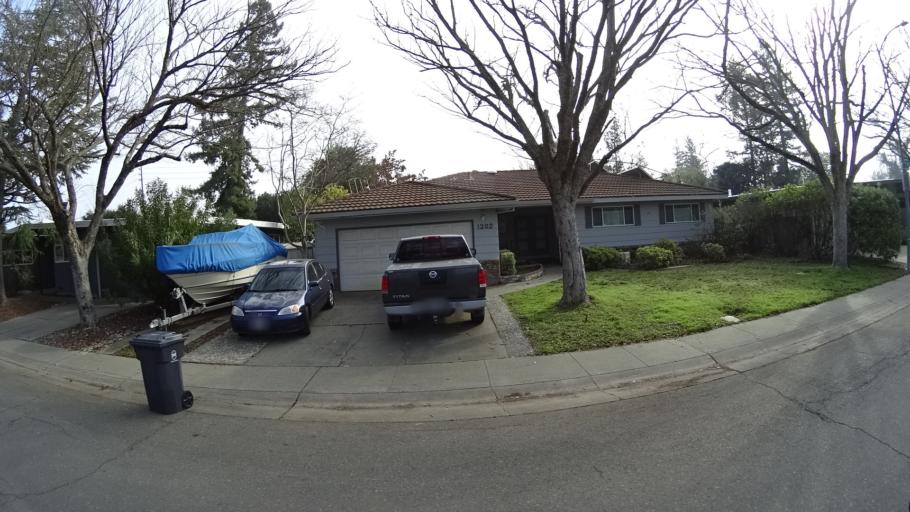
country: US
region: California
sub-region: Yolo County
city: Davis
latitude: 38.5543
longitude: -121.7625
